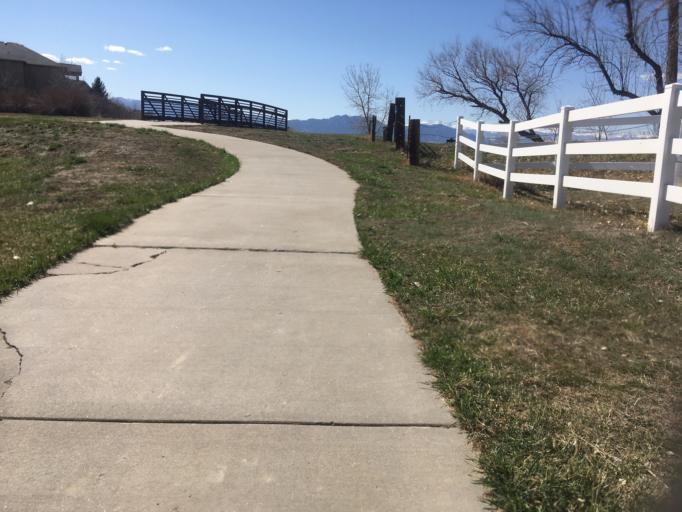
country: US
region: Colorado
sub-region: Broomfield County
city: Broomfield
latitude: 39.9505
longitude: -105.0682
